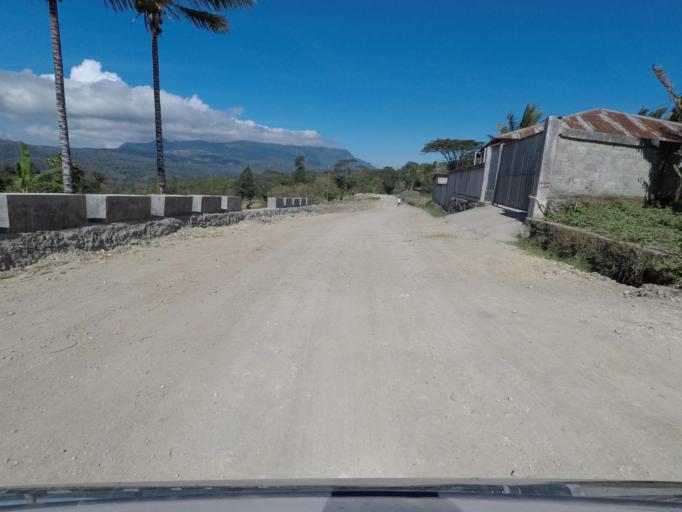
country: TL
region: Baucau
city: Venilale
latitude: -8.6454
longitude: 126.3751
